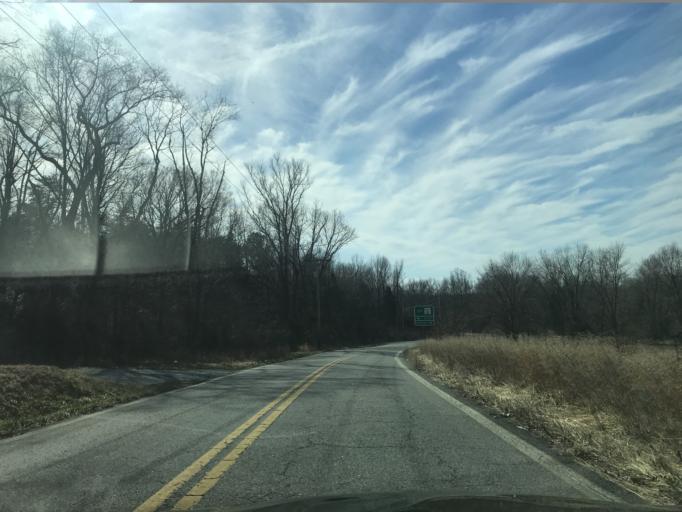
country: US
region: Virginia
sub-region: Prince William County
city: Quantico Station
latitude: 38.4418
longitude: -77.1968
